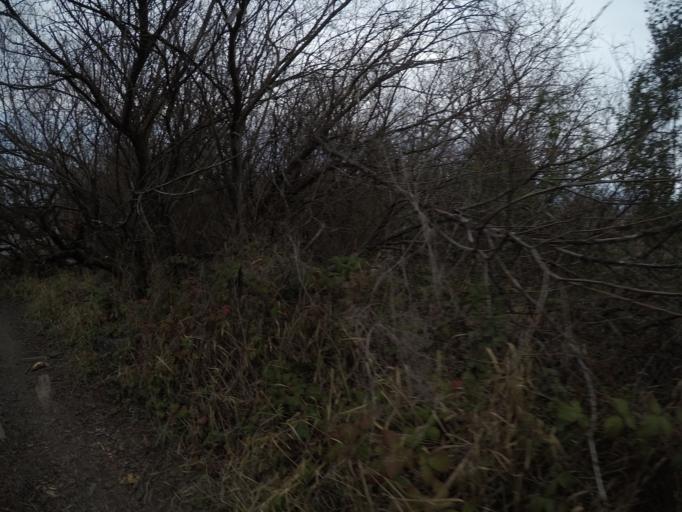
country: US
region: California
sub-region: Santa Cruz County
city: Scotts Valley
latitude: 37.0663
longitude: -122.0070
